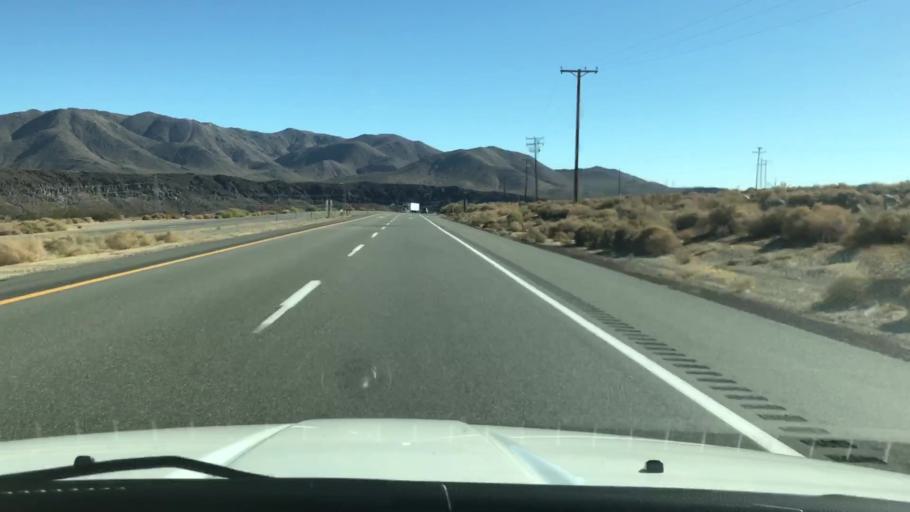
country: US
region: California
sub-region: Kern County
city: Inyokern
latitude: 35.9594
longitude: -117.9134
